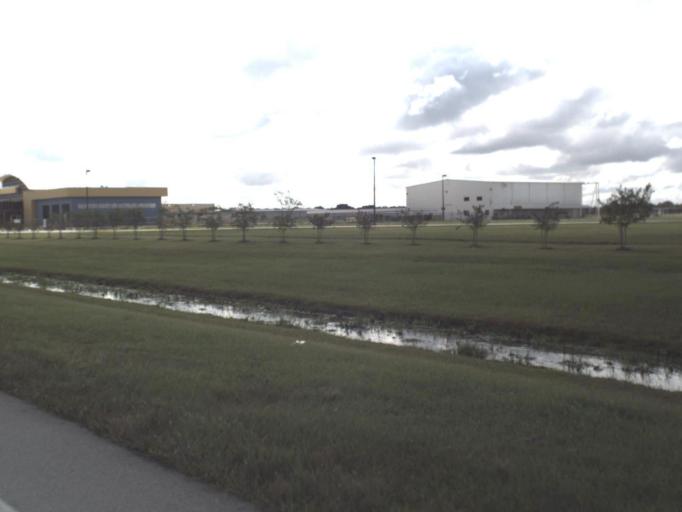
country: US
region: Florida
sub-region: Polk County
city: Winston
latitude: 27.9966
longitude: -82.0122
